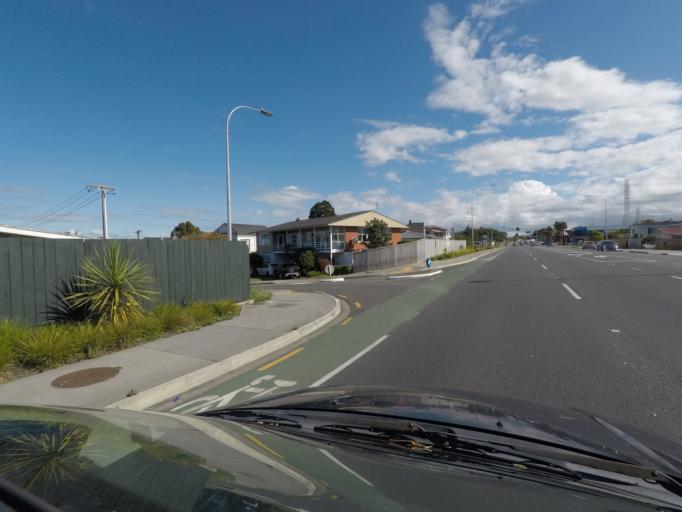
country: NZ
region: Auckland
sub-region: Auckland
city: Rosebank
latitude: -36.8613
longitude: 174.6499
